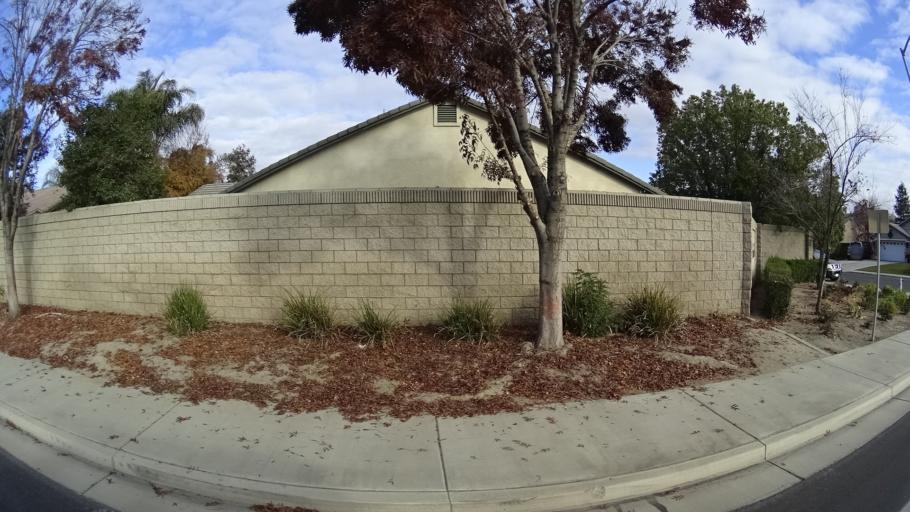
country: US
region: California
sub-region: Kern County
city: Greenacres
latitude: 35.3035
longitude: -119.1061
